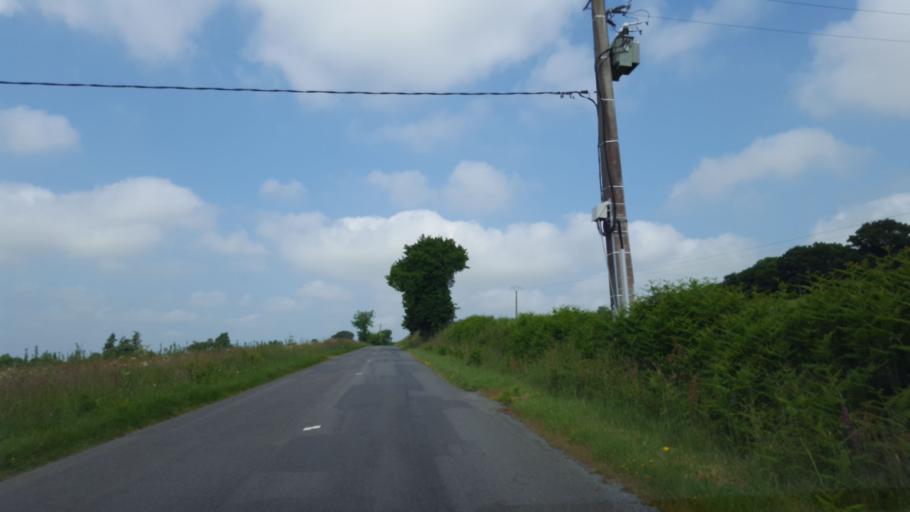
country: FR
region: Brittany
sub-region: Departement d'Ille-et-Vilaine
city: Baulon
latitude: 47.9273
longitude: -1.9295
